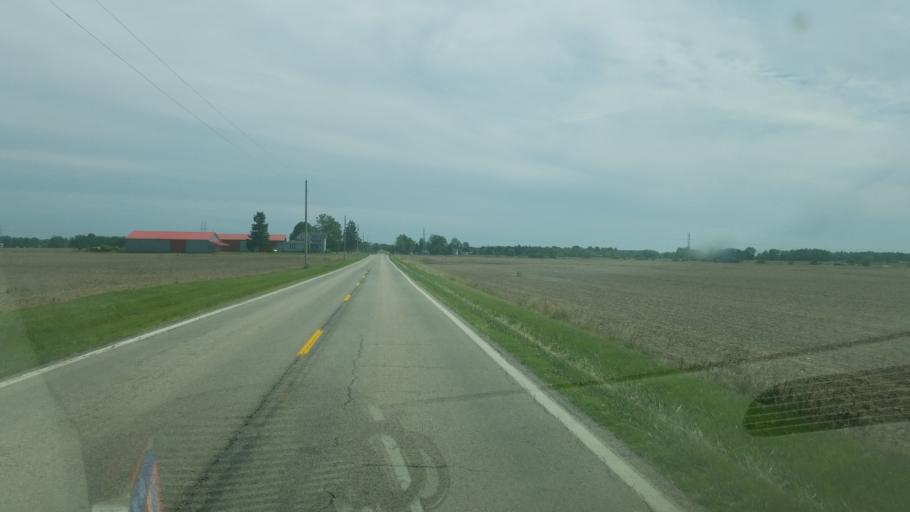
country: US
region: Ohio
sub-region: Morrow County
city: Cardington
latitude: 40.4961
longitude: -82.9632
